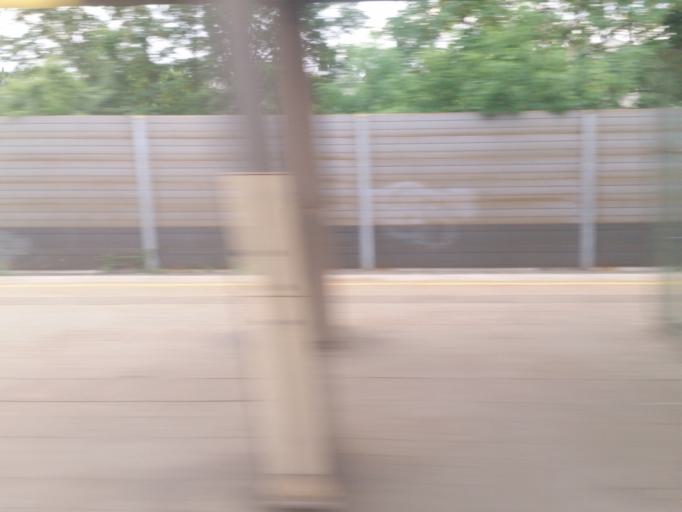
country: AT
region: Lower Austria
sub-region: Politischer Bezirk Wien-Umgebung
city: Schwechat
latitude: 48.1694
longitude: 16.4186
